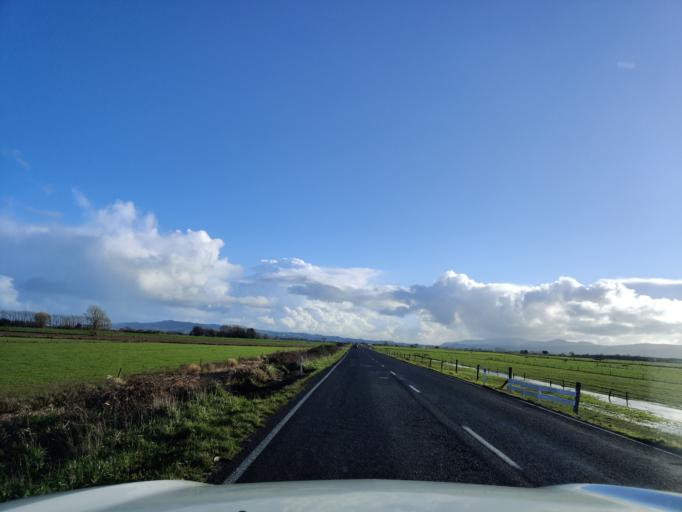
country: NZ
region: Waikato
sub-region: Hauraki District
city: Paeroa
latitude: -37.4947
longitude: 175.5819
